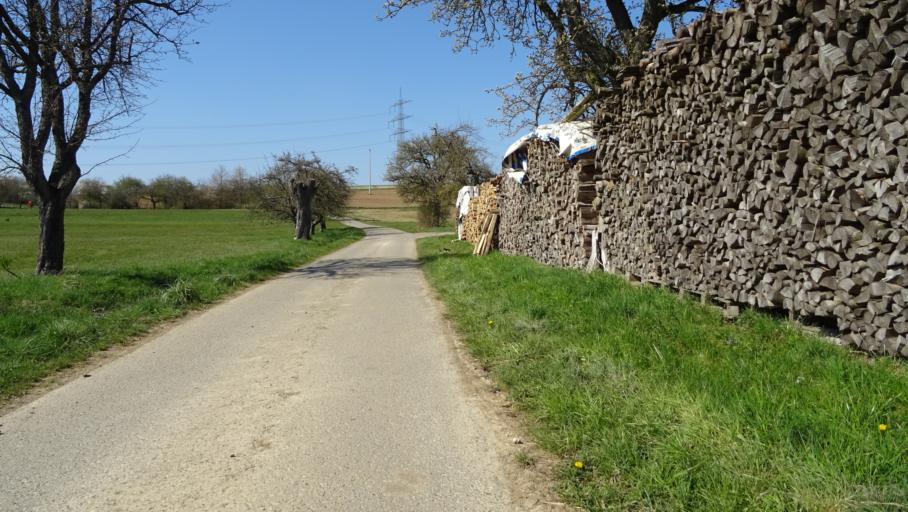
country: DE
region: Baden-Wuerttemberg
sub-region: Karlsruhe Region
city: Billigheim
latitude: 49.4050
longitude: 9.2641
